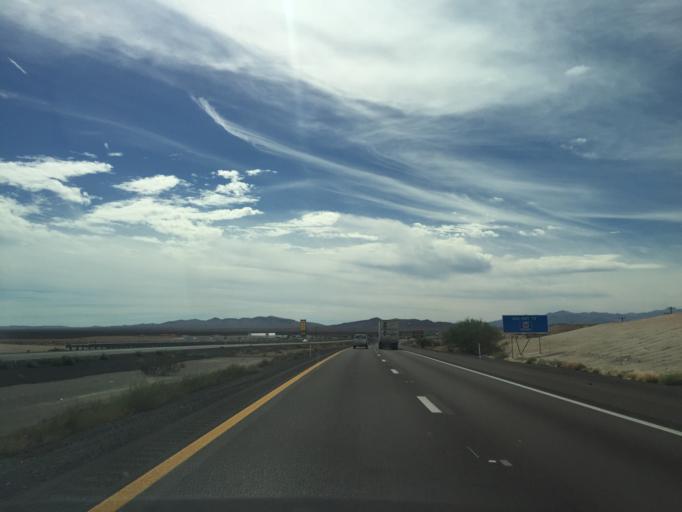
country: US
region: Nevada
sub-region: Clark County
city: Moapa Town
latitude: 36.5082
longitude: -114.7517
